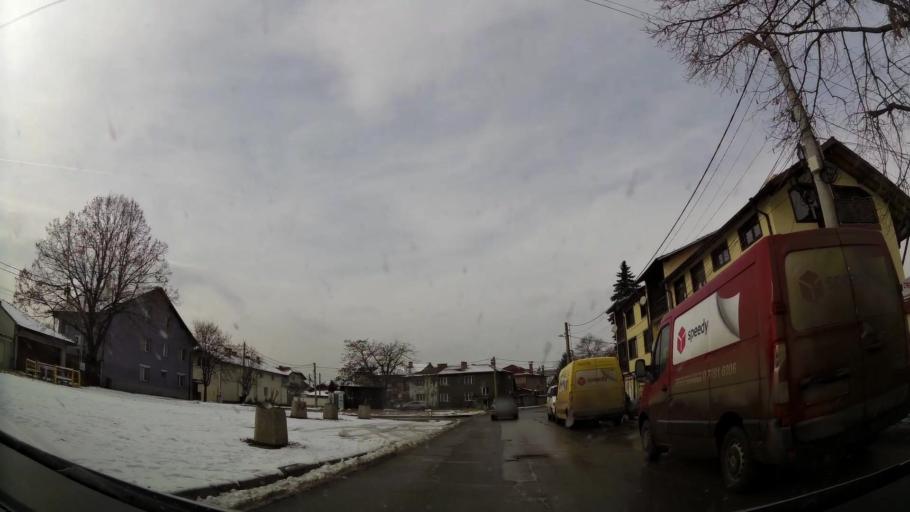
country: BG
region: Sofia-Capital
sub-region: Stolichna Obshtina
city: Sofia
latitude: 42.7129
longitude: 23.4197
